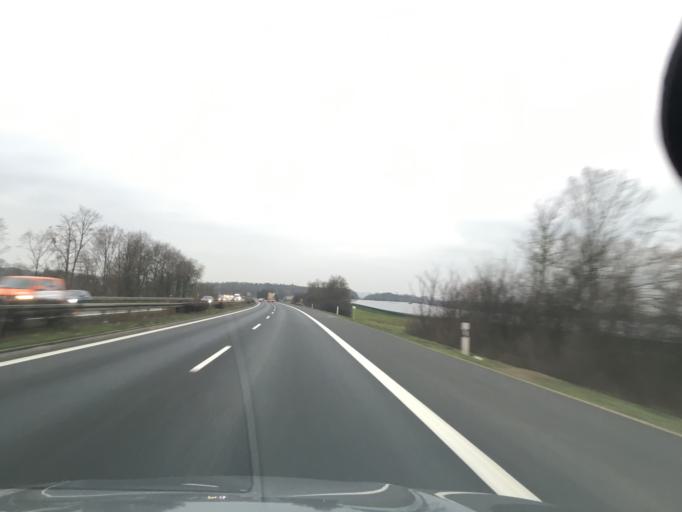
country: DE
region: Bavaria
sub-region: Regierungsbezirk Unterfranken
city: Kleinlangheim
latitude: 49.7814
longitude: 10.2926
